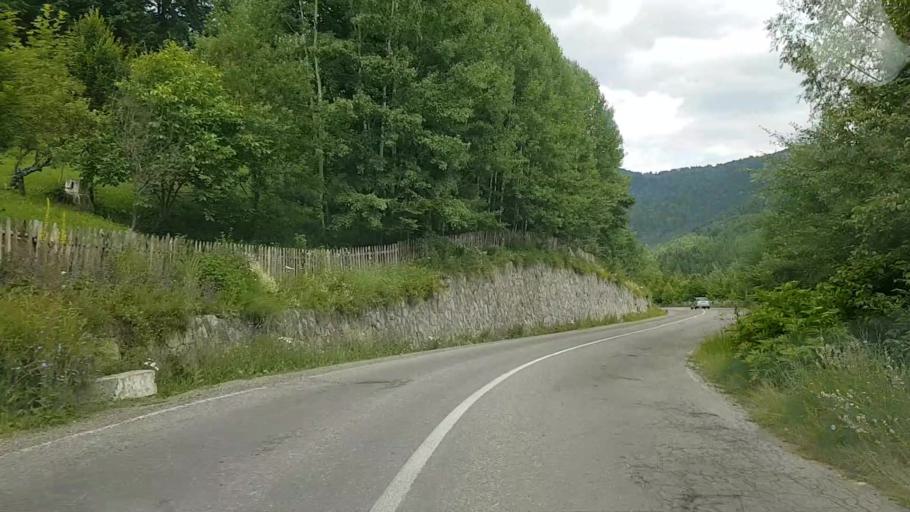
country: RO
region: Neamt
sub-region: Comuna Bicaz
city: Dodeni
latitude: 46.9891
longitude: 26.1089
